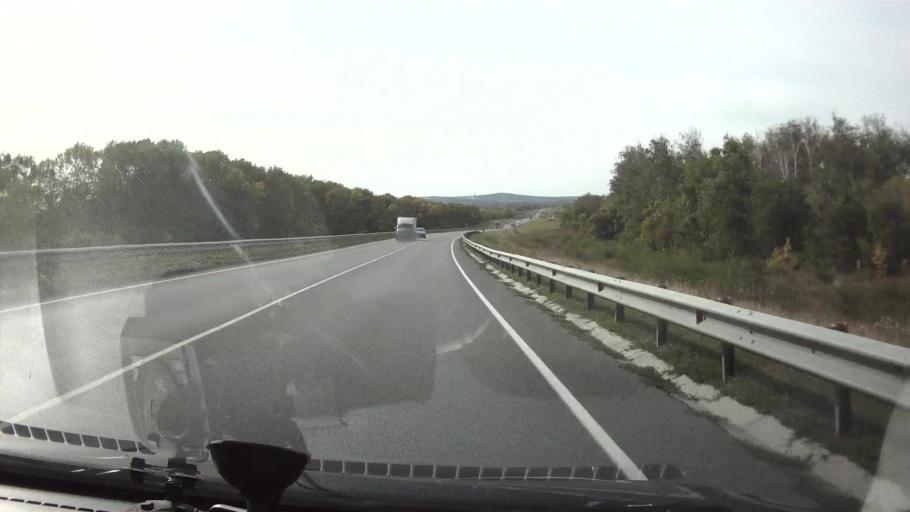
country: RU
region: Saratov
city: Tersa
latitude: 52.0828
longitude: 47.6680
